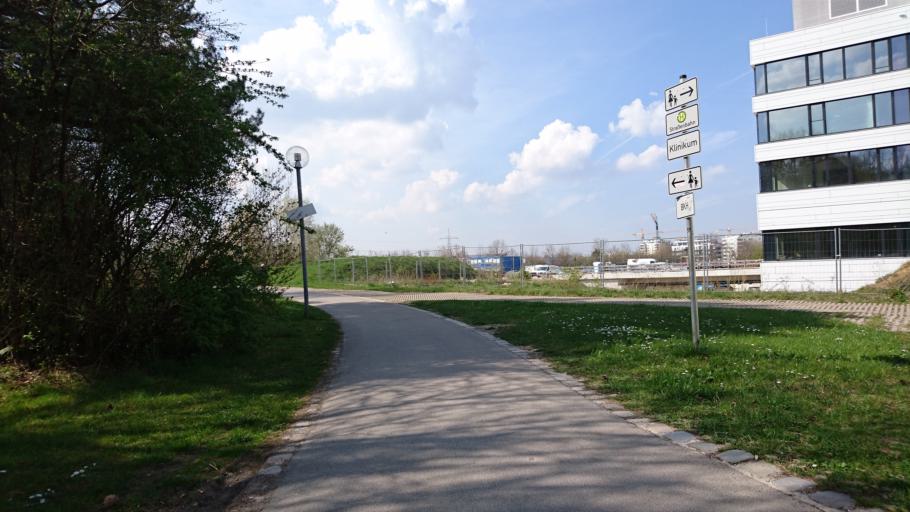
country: DE
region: Bavaria
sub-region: Swabia
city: Stadtbergen
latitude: 48.3836
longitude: 10.8368
